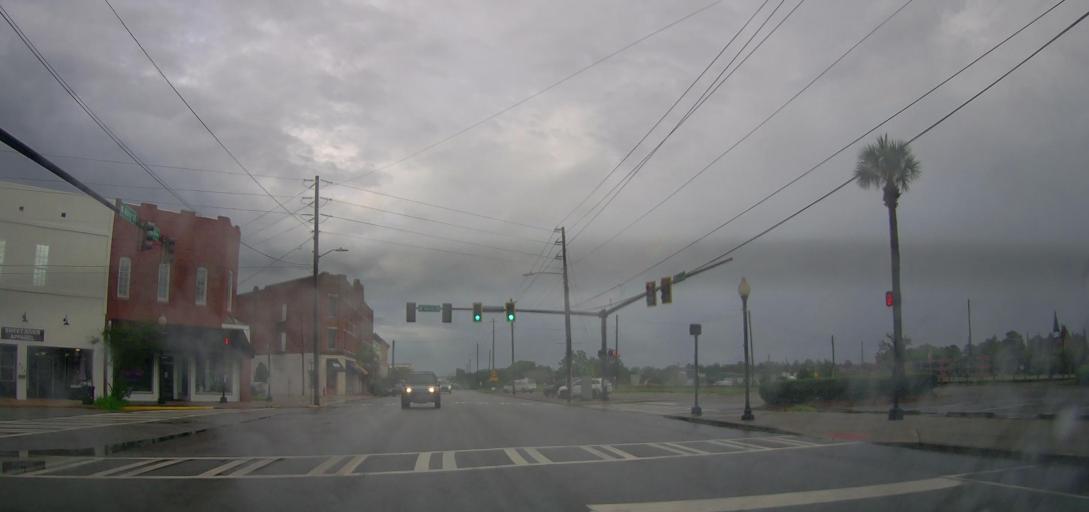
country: US
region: Georgia
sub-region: Ware County
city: Waycross
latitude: 31.2102
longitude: -82.3584
